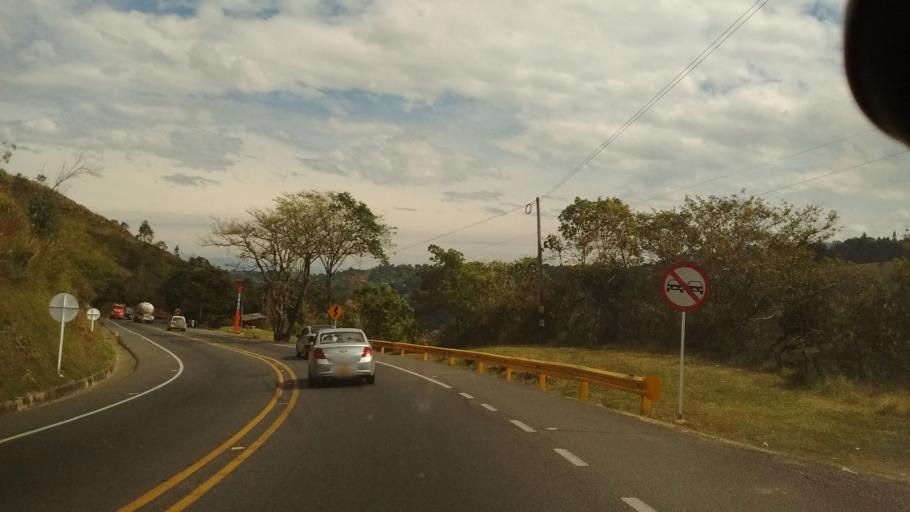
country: CO
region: Cauca
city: Cajibio
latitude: 2.6155
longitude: -76.5145
